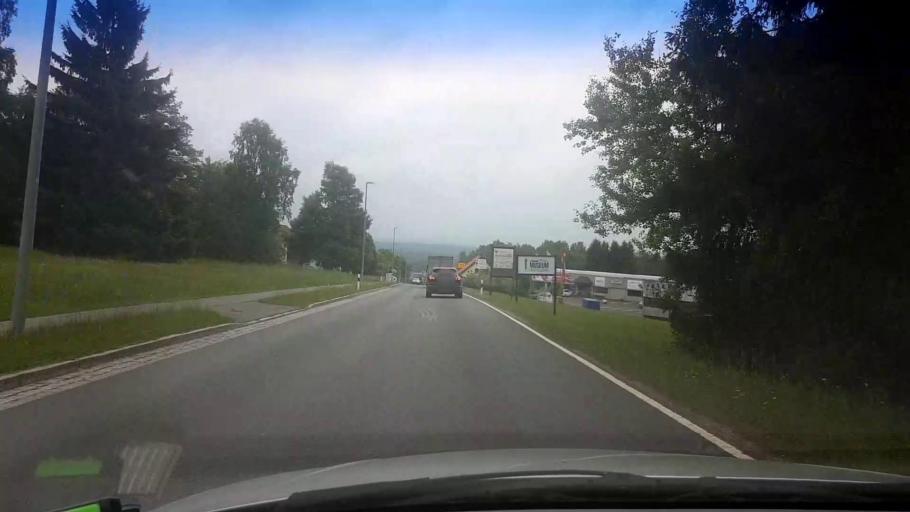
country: DE
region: Bavaria
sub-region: Upper Franconia
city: Fichtelberg
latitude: 50.0022
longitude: 11.8408
